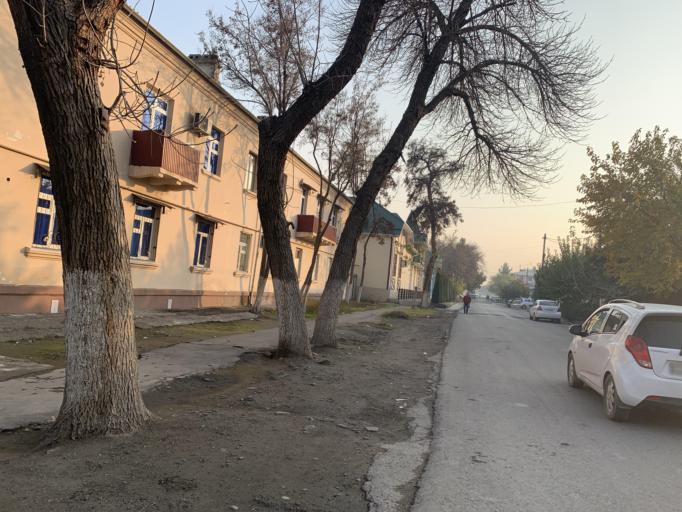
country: UZ
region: Fergana
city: Qo`qon
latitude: 40.5216
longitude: 70.9381
